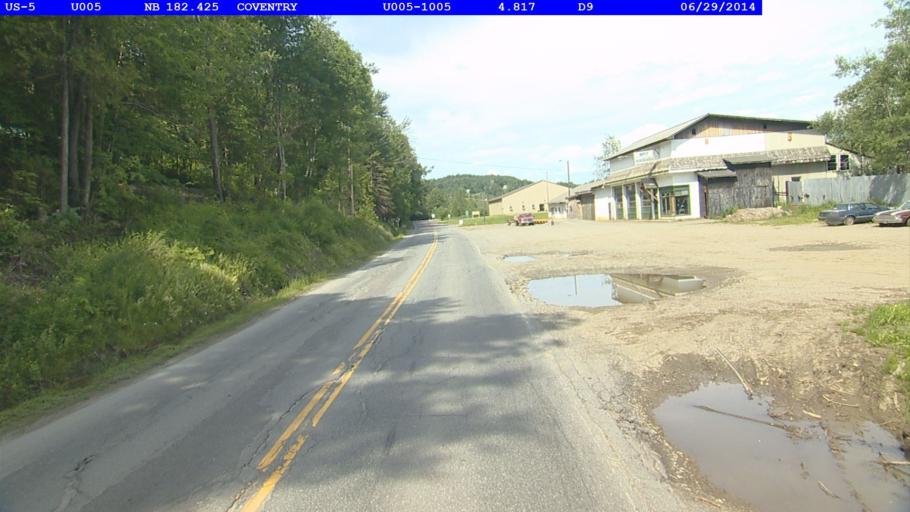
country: US
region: Vermont
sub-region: Orleans County
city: Newport
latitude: 44.9224
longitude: -72.2304
